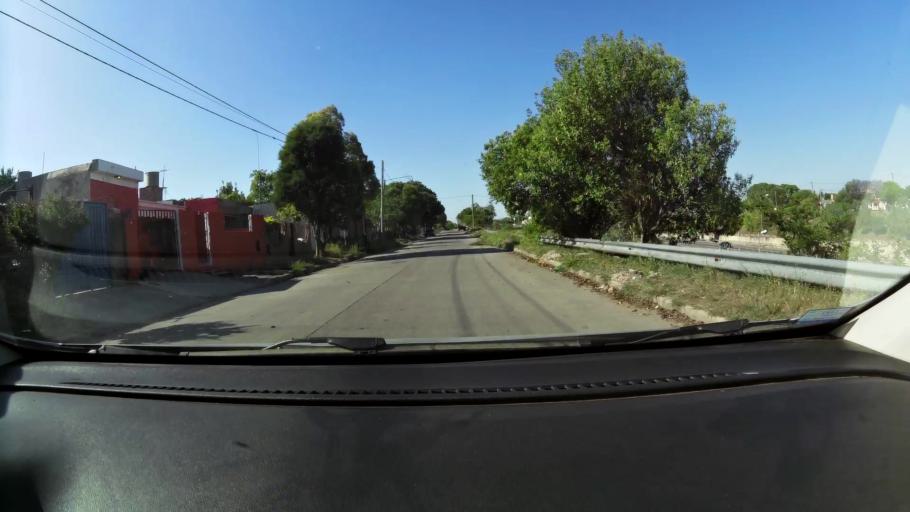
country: AR
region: Cordoba
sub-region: Departamento de Capital
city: Cordoba
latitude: -31.3921
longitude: -64.1277
